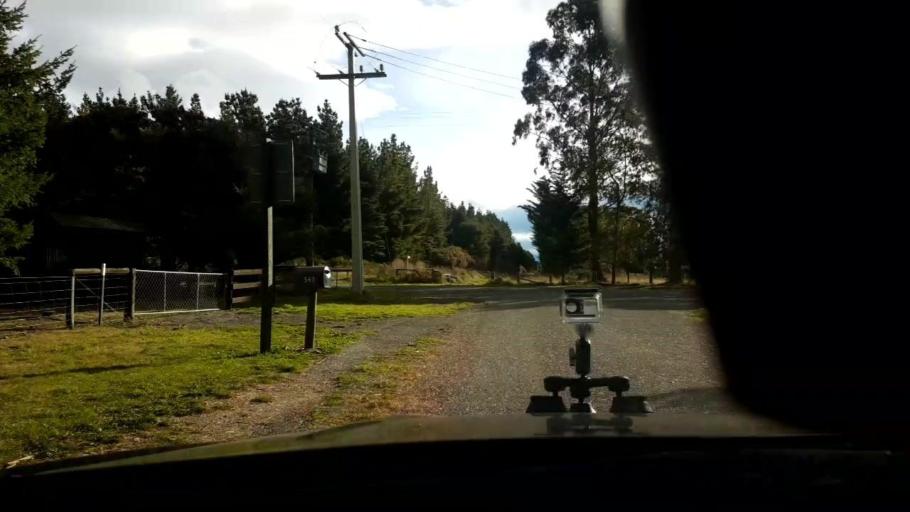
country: NZ
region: Canterbury
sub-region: Waimakariri District
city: Oxford
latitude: -43.3924
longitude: 172.2905
